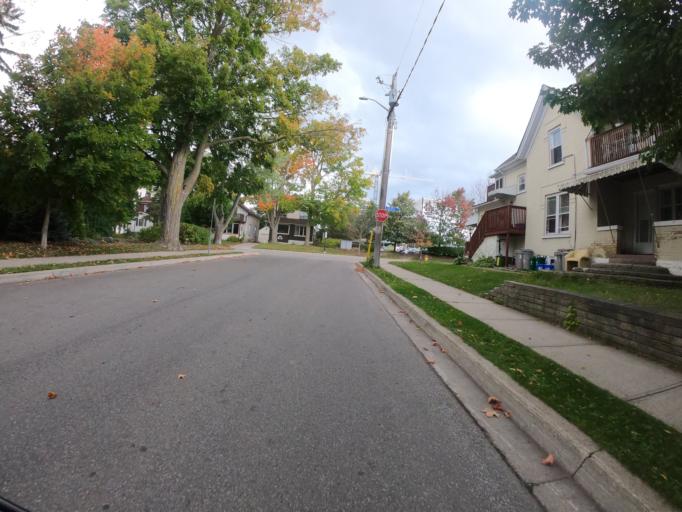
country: CA
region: Ontario
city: Waterloo
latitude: 43.4498
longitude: -80.4970
